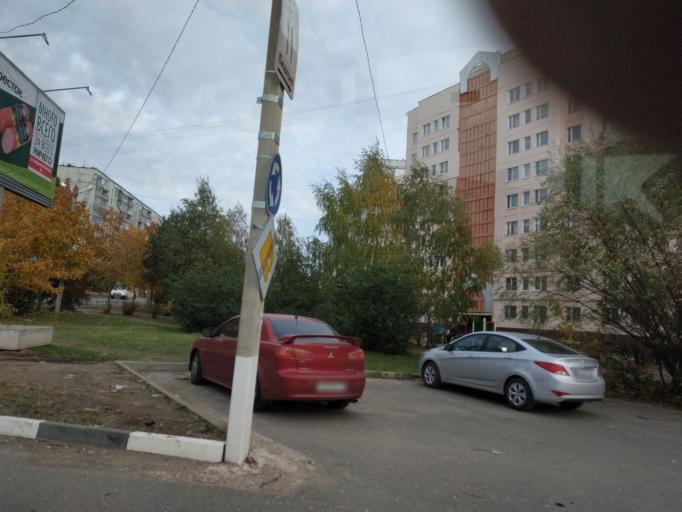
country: RU
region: Moskovskaya
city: Mozhaysk
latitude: 55.4979
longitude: 36.0334
